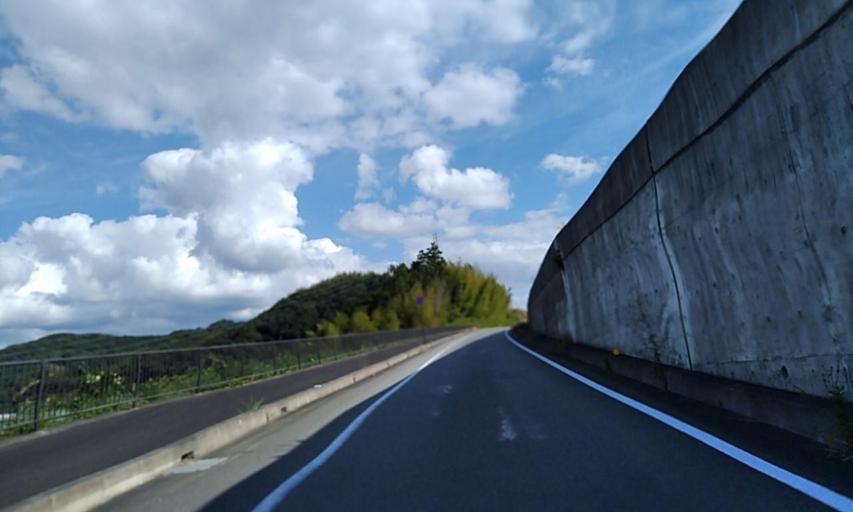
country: JP
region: Wakayama
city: Tanabe
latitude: 33.7516
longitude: 135.3546
